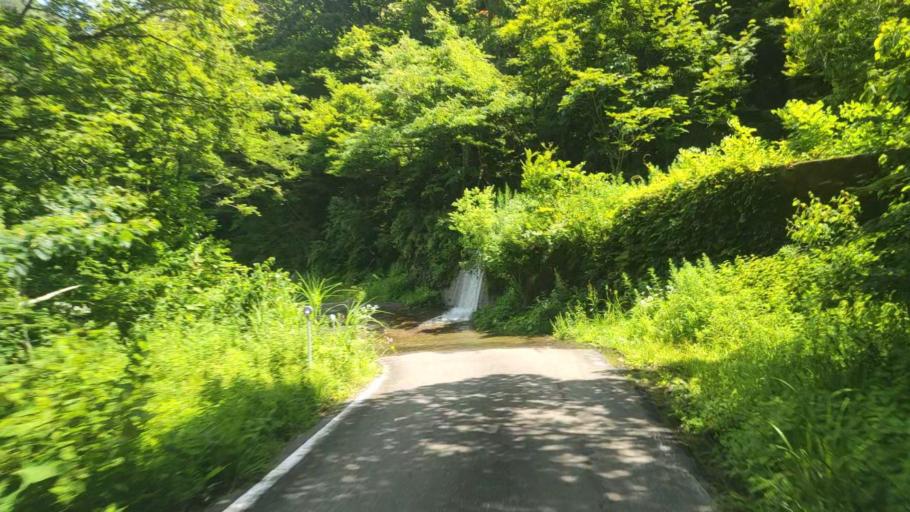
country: JP
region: Fukui
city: Ono
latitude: 35.7619
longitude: 136.5551
